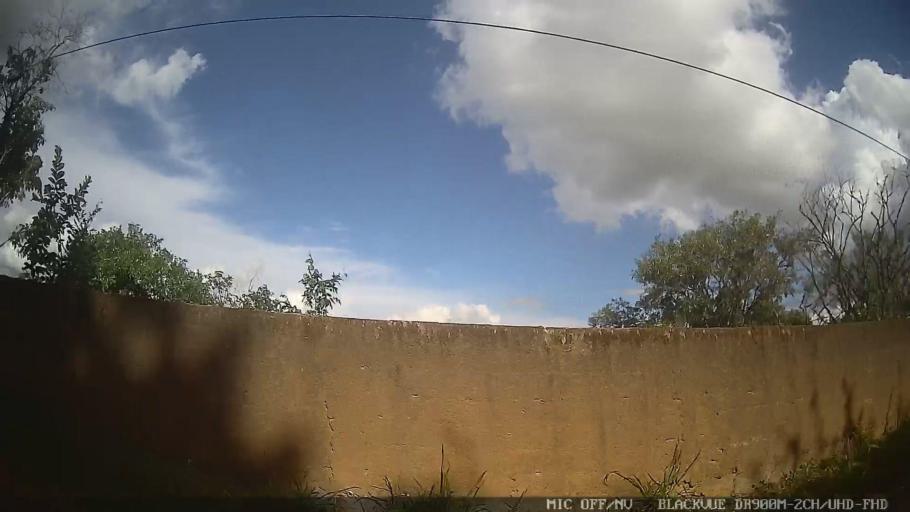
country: BR
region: Sao Paulo
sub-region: Bom Jesus Dos Perdoes
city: Bom Jesus dos Perdoes
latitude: -23.1205
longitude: -46.4950
